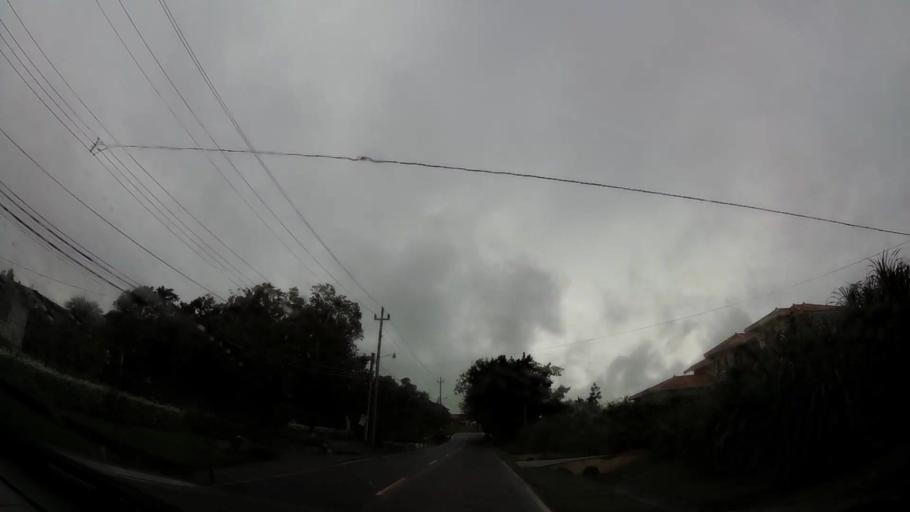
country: PA
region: Veraguas
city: Santiago de Veraguas
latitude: 8.0921
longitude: -80.9572
